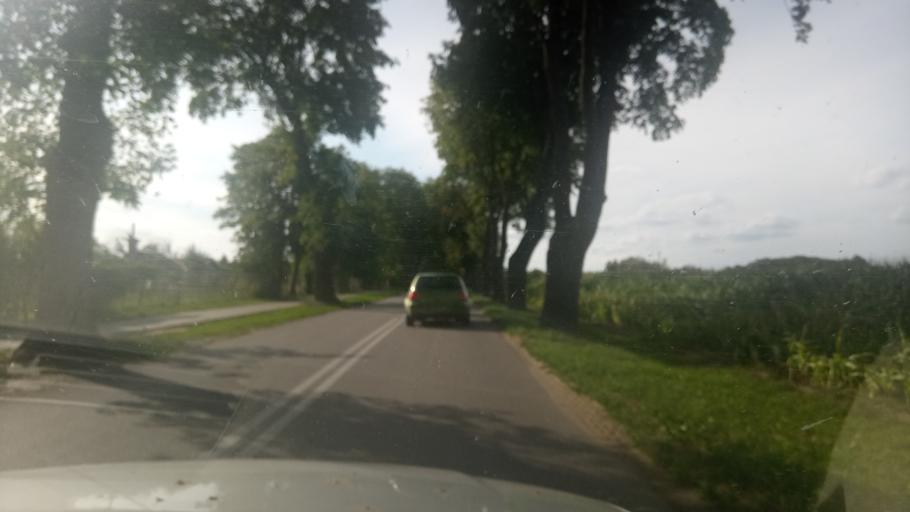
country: PL
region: Greater Poland Voivodeship
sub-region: Powiat pilski
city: Lobzenica
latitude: 53.2544
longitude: 17.2669
